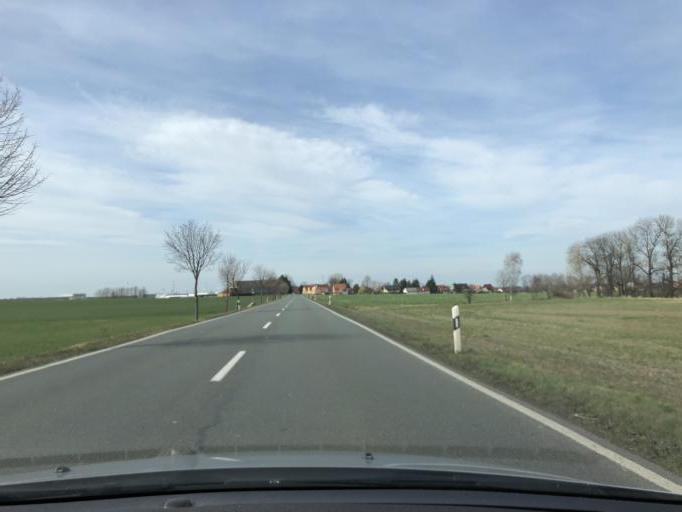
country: DE
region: Saxony-Anhalt
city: Osterfeld
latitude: 51.0835
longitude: 11.9735
